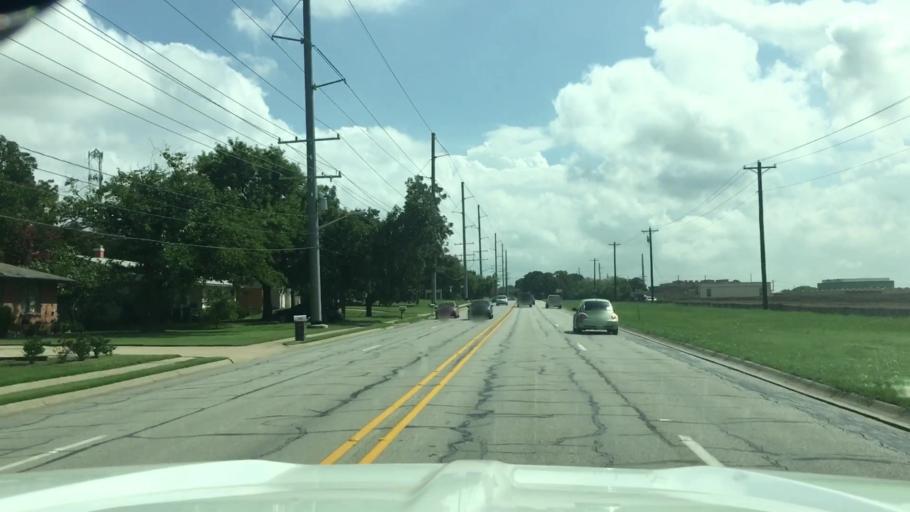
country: US
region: Texas
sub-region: Denton County
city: Denton
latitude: 33.2233
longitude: -97.1612
